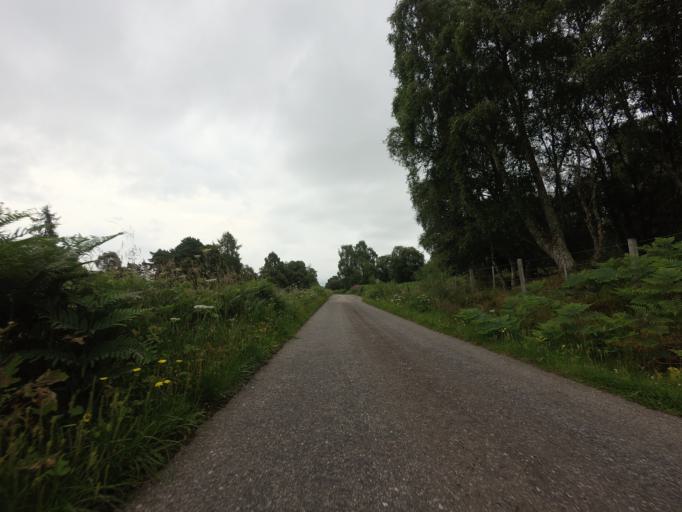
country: GB
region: Scotland
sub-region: Highland
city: Evanton
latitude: 57.9057
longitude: -4.3916
